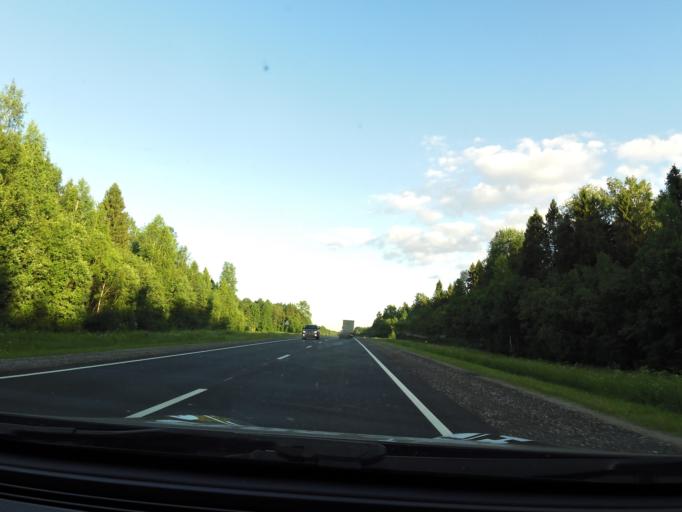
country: RU
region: Vologda
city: Gryazovets
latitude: 58.9990
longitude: 40.1297
